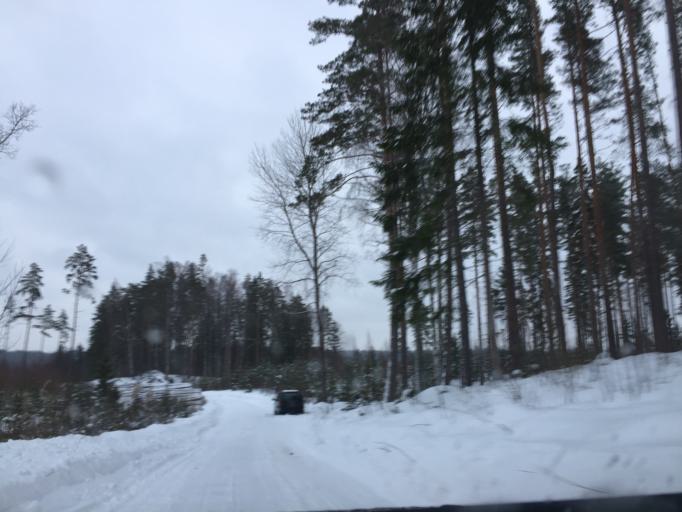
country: LV
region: Amatas Novads
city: Drabesi
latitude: 57.2013
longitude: 25.2968
